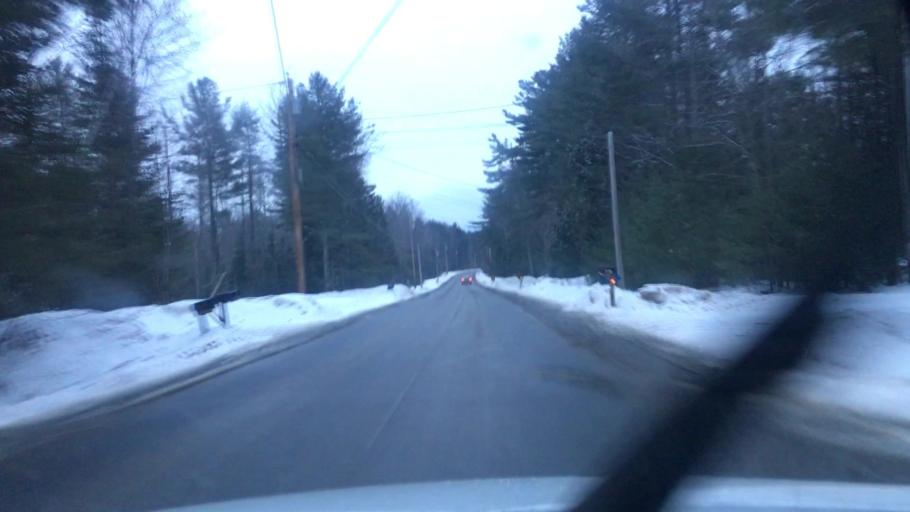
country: US
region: Maine
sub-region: Kennebec County
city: Oakland
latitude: 44.6235
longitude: -69.7265
